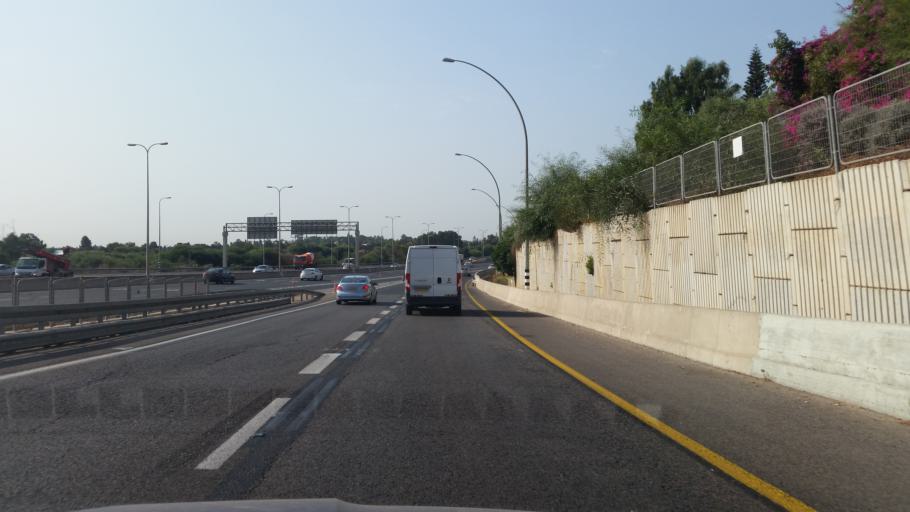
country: IL
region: Central District
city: Even Yehuda
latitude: 32.2724
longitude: 34.8529
